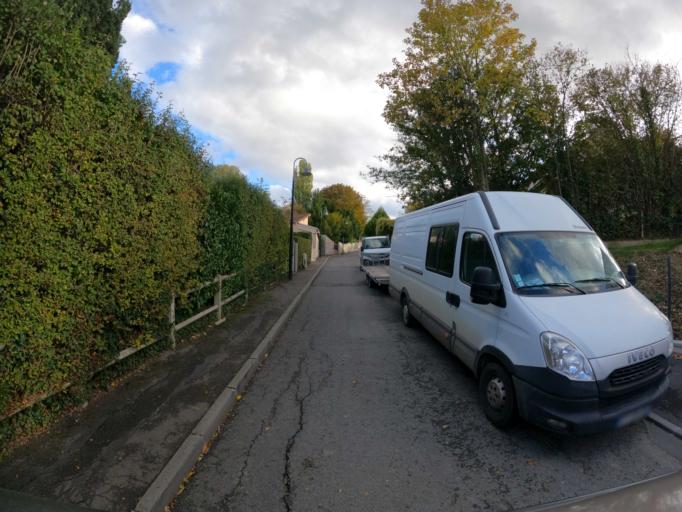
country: FR
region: Ile-de-France
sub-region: Departement de Seine-et-Marne
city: Chessy
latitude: 48.8811
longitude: 2.7610
